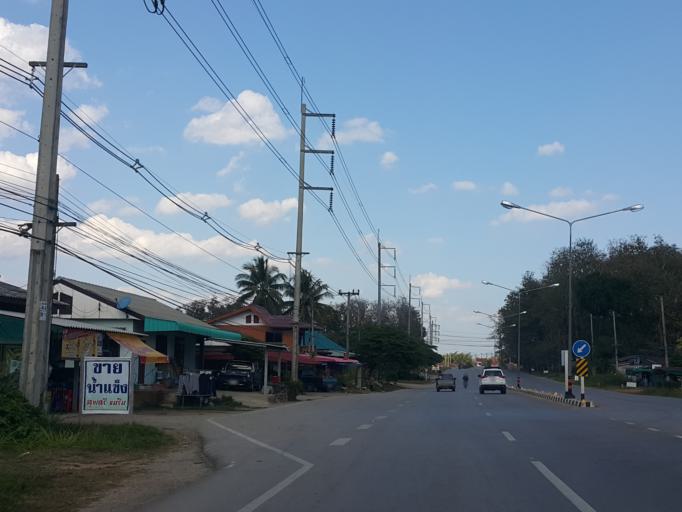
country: TH
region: Chiang Mai
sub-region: Amphoe Chiang Dao
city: Chiang Dao
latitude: 19.3338
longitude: 98.9566
